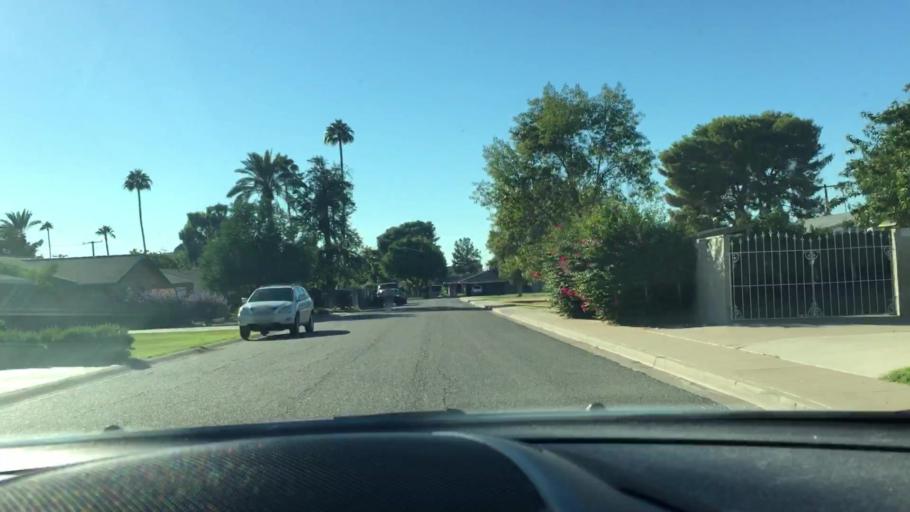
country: US
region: Arizona
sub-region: Maricopa County
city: Paradise Valley
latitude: 33.4834
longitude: -111.9812
